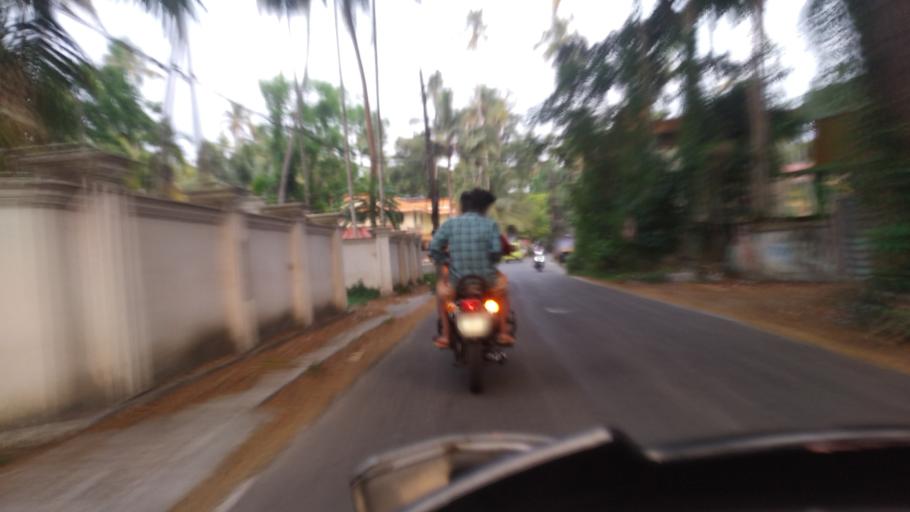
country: IN
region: Kerala
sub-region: Thrissur District
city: Kodungallur
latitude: 10.1662
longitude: 76.2020
